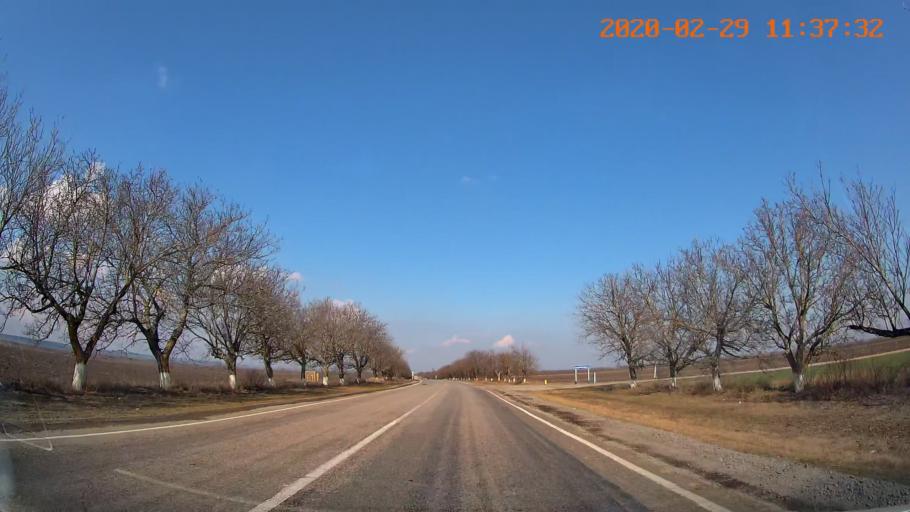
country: MD
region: Rezina
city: Saharna
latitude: 47.6130
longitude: 29.0453
